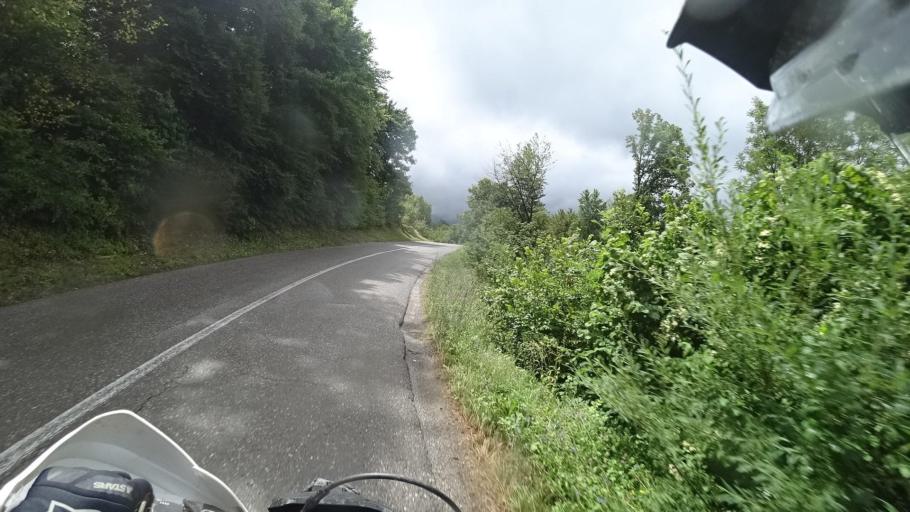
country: HR
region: Karlovacka
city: Plaski
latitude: 45.0298
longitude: 15.4151
